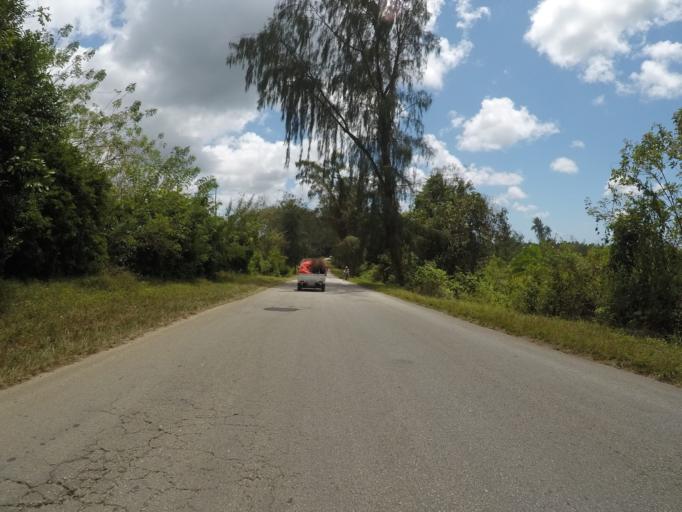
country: TZ
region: Zanzibar Central/South
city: Mahonda
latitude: -6.2810
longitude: 39.4154
